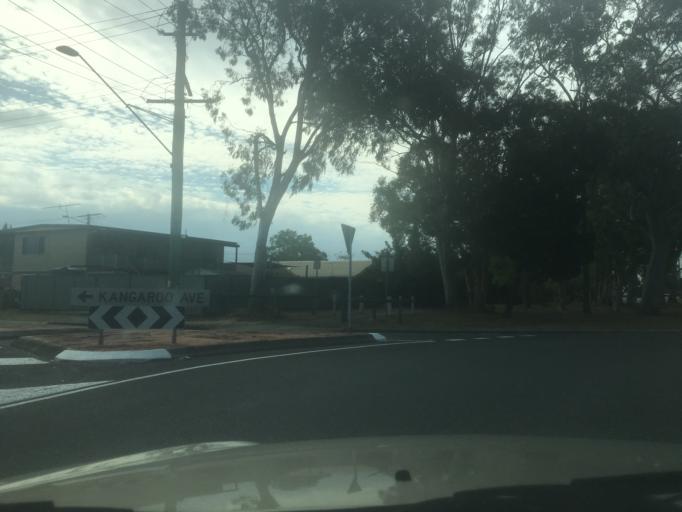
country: AU
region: Queensland
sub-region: Moreton Bay
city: Bongaree
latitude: -27.0745
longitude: 153.1635
